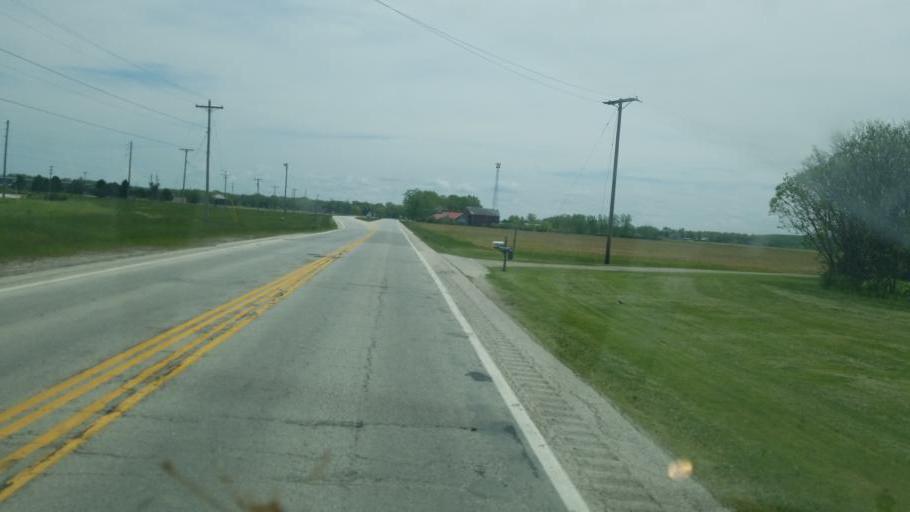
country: US
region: Ohio
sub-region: Ottawa County
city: Oak Harbor
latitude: 41.5434
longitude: -83.0447
